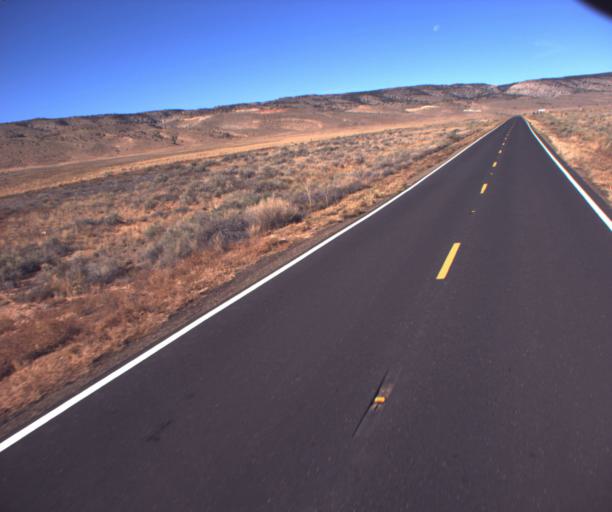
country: US
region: Arizona
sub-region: Coconino County
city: Fredonia
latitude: 36.7268
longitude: -112.0316
